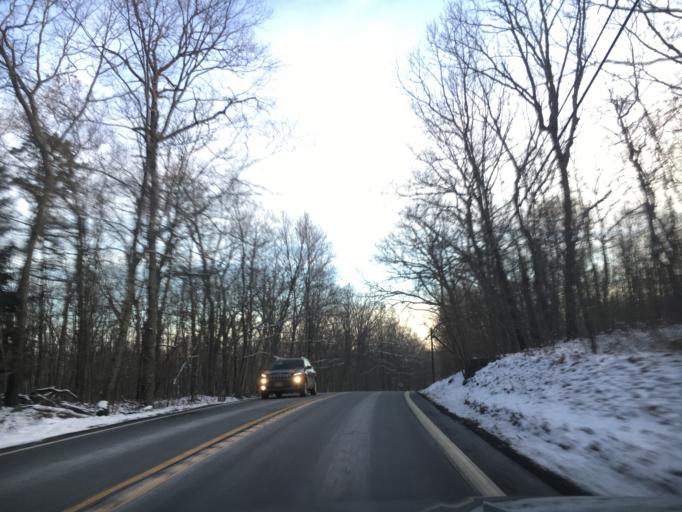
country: US
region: Pennsylvania
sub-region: Pike County
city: Saw Creek
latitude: 41.1584
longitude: -75.0825
